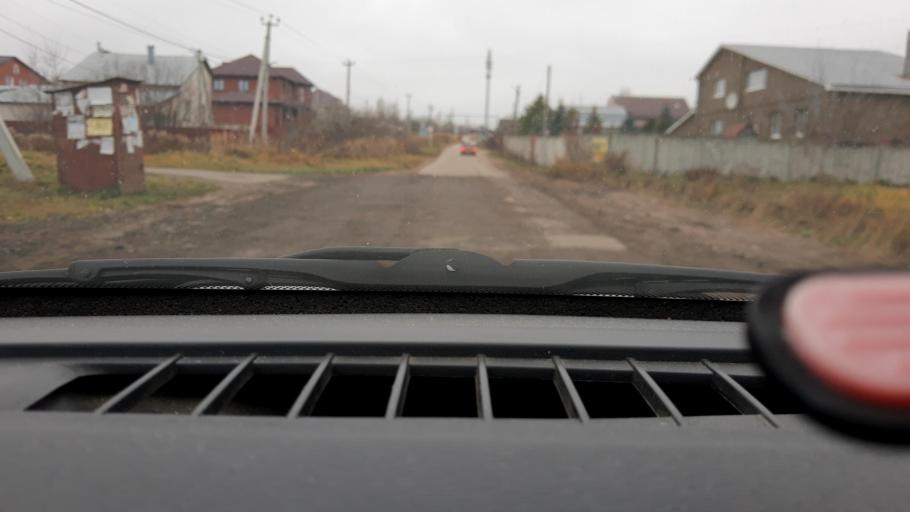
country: RU
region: Nizjnij Novgorod
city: Burevestnik
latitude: 56.1840
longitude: 43.9161
